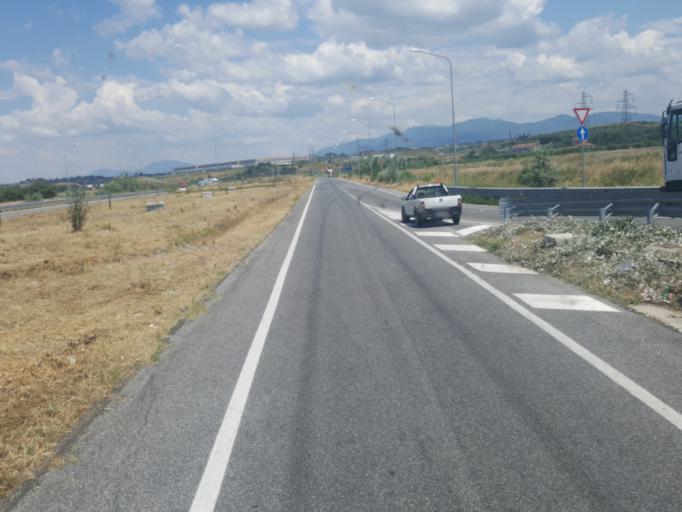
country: IT
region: Latium
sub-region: Citta metropolitana di Roma Capitale
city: Fiano Romano
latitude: 42.1539
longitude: 12.6423
